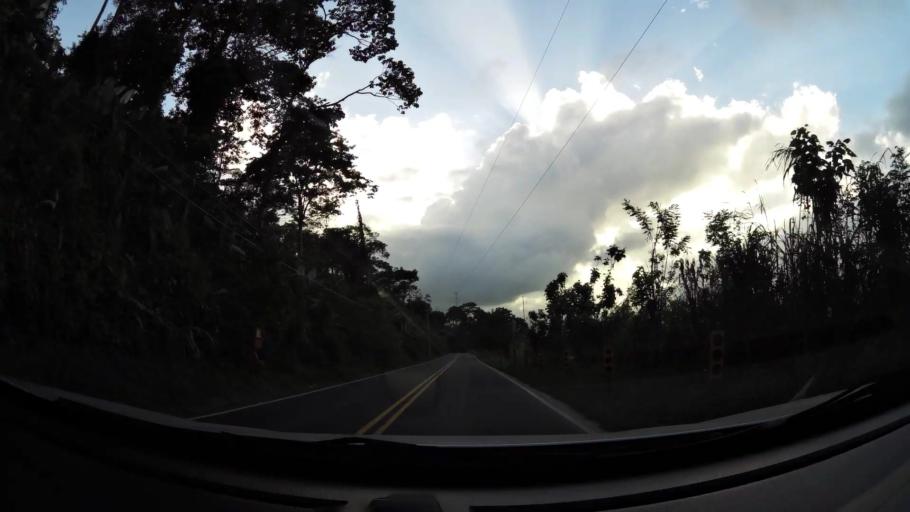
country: CR
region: Limon
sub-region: Canton de Siquirres
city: Siquirres
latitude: 10.0076
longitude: -83.5682
